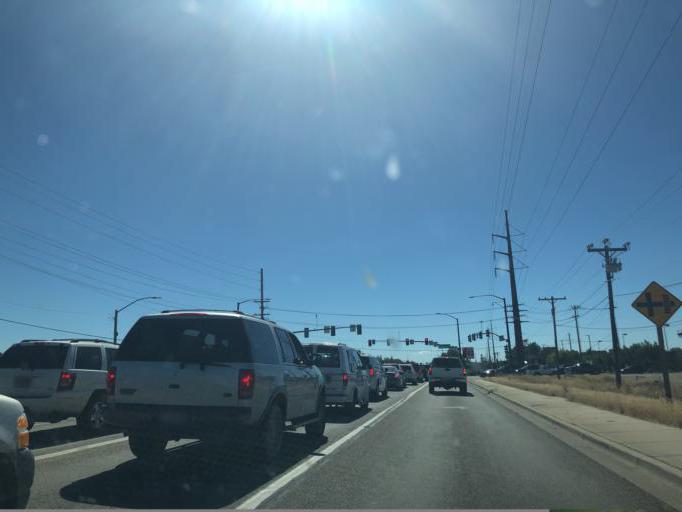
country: US
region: Idaho
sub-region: Ada County
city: Garden City
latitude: 43.6051
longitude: -116.2801
